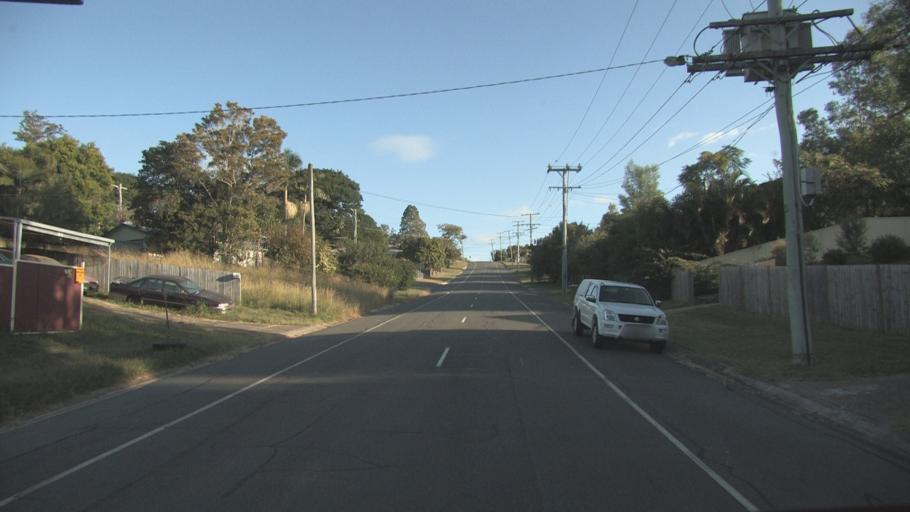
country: AU
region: Queensland
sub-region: Logan
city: Beenleigh
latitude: -27.7061
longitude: 153.1777
